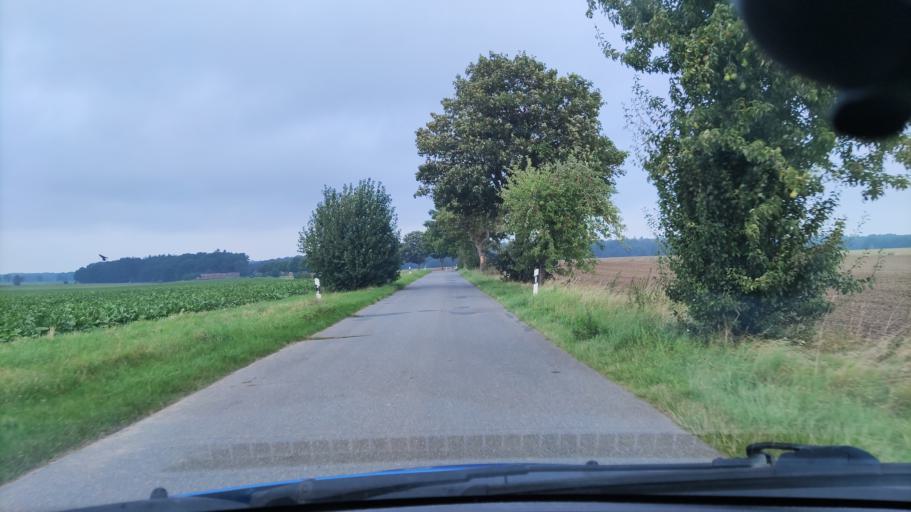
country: DE
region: Lower Saxony
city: Altenmedingen
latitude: 53.1353
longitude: 10.5995
